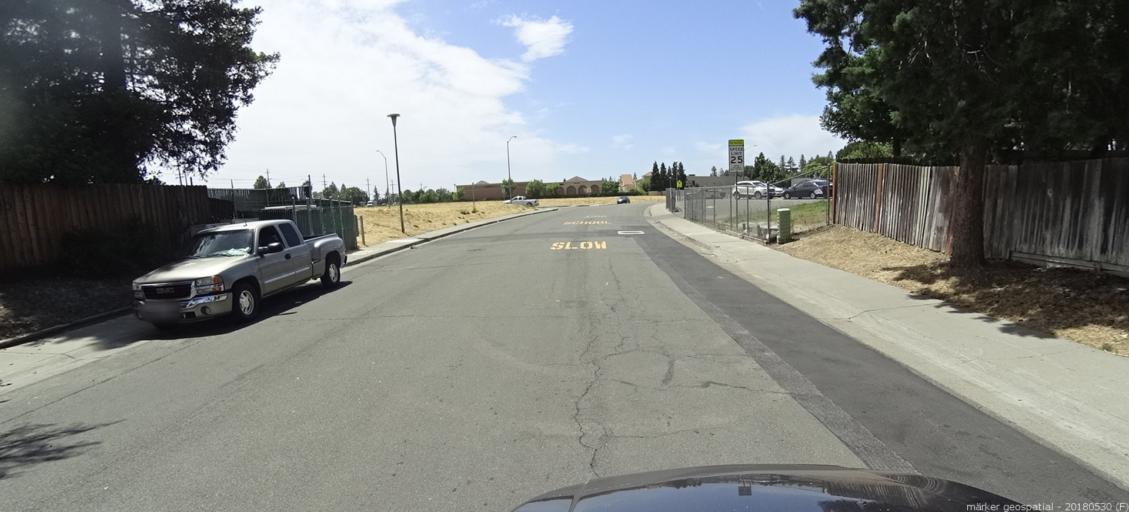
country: US
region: California
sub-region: Sacramento County
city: Sacramento
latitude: 38.6342
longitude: -121.4766
